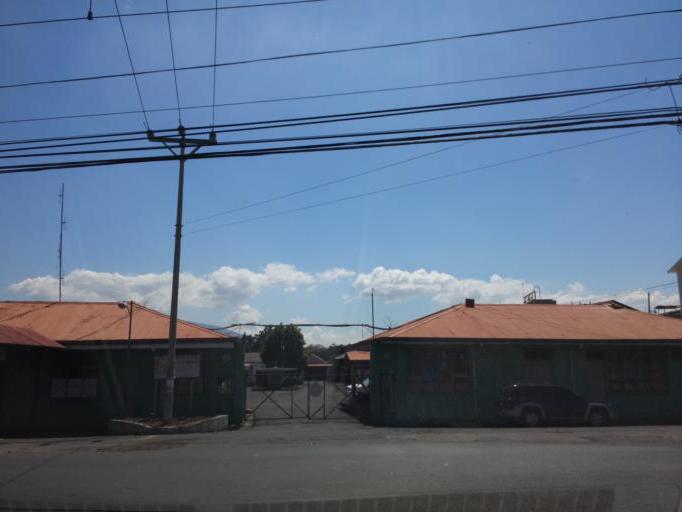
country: CR
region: Alajuela
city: Alajuela
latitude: 10.0049
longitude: -84.2270
